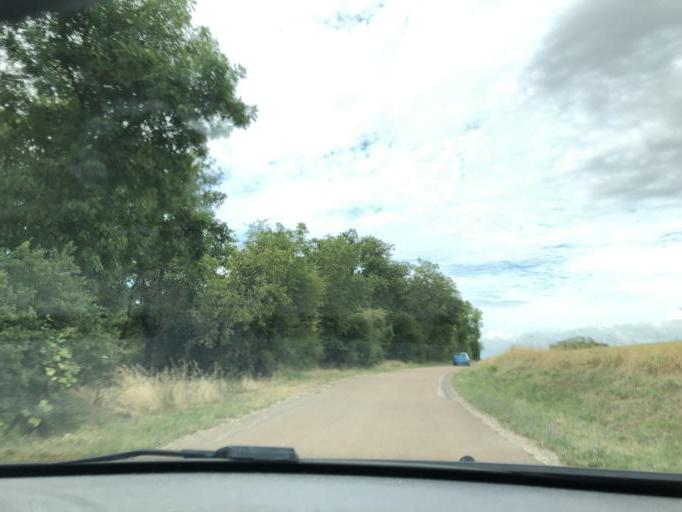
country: FR
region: Bourgogne
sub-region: Departement de l'Yonne
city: Chablis
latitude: 47.7828
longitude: 3.8335
